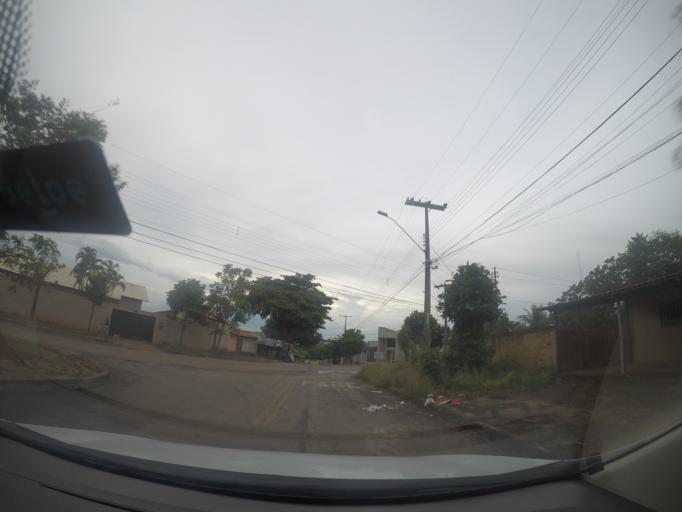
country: BR
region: Goias
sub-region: Goiania
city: Goiania
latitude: -16.6373
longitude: -49.2416
